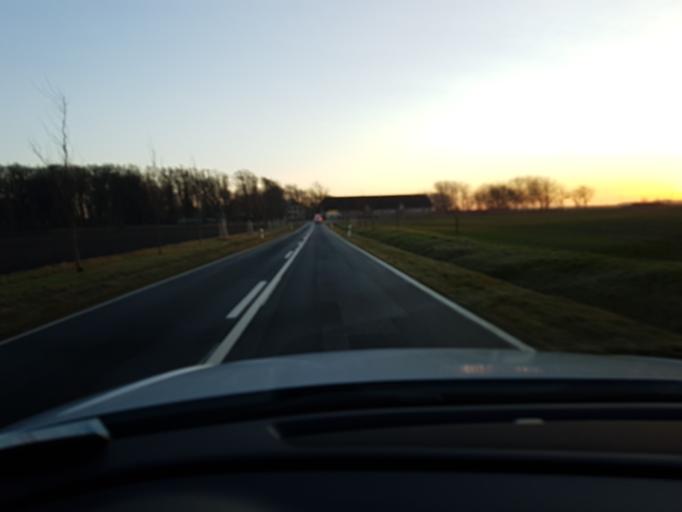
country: DE
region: Mecklenburg-Vorpommern
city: Wiek
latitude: 54.5889
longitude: 13.2884
